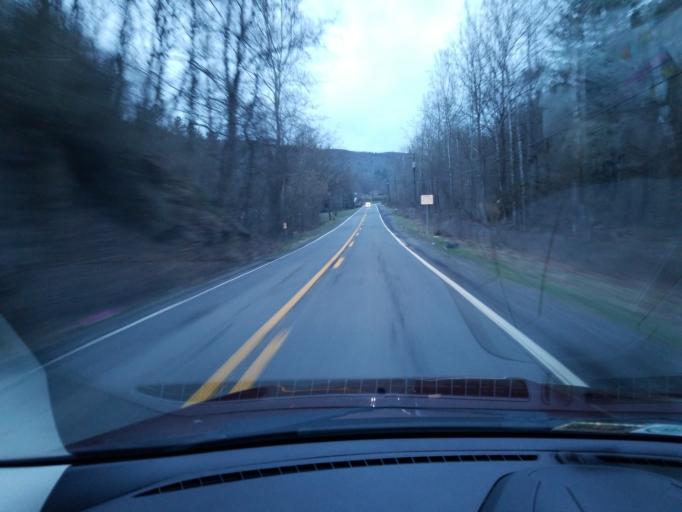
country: US
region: West Virginia
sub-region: Greenbrier County
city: Lewisburg
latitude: 37.7729
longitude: -80.3938
